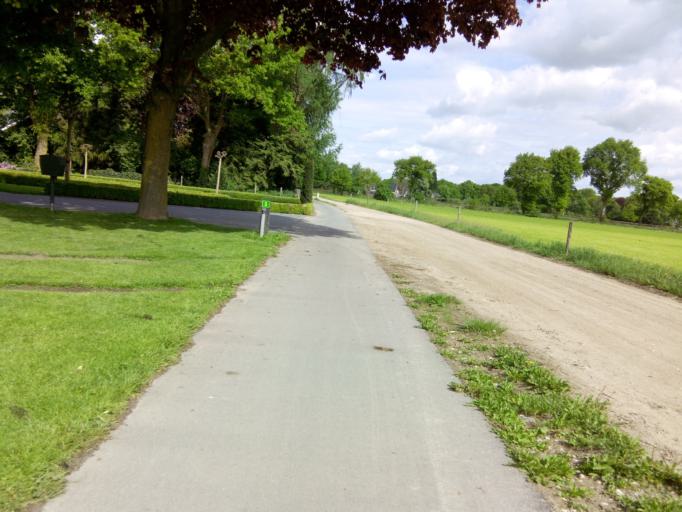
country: NL
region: Gelderland
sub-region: Gemeente Ede
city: Lunteren
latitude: 52.0758
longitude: 5.6434
